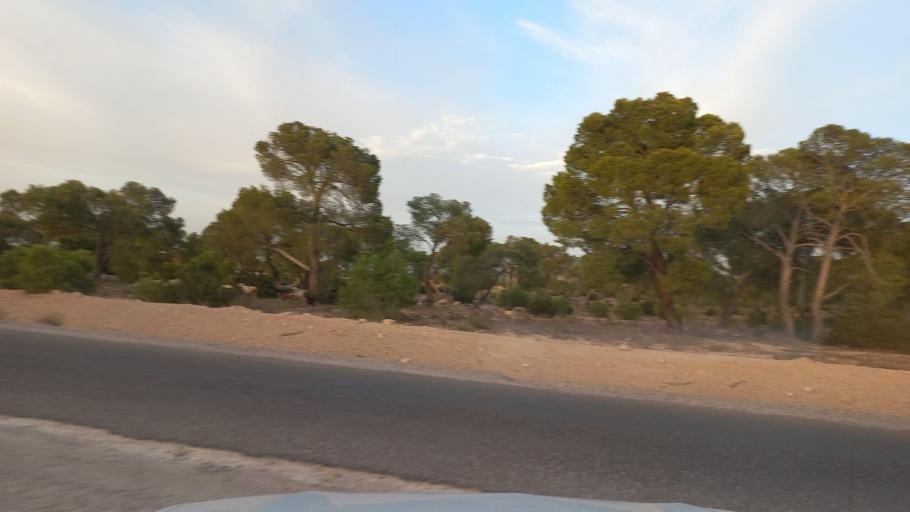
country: TN
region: Al Qasrayn
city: Sbiba
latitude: 35.4268
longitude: 8.9199
